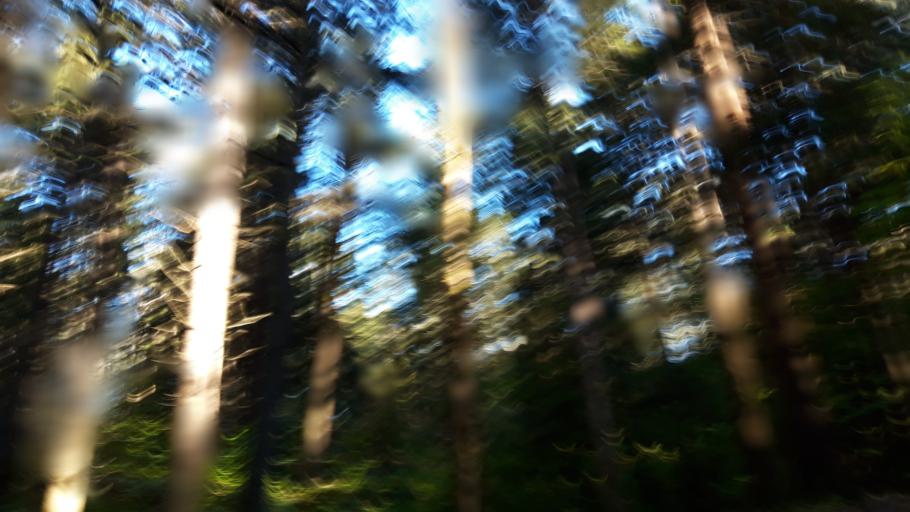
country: RU
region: Moscow
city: Zelenograd
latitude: 55.9853
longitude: 37.1968
